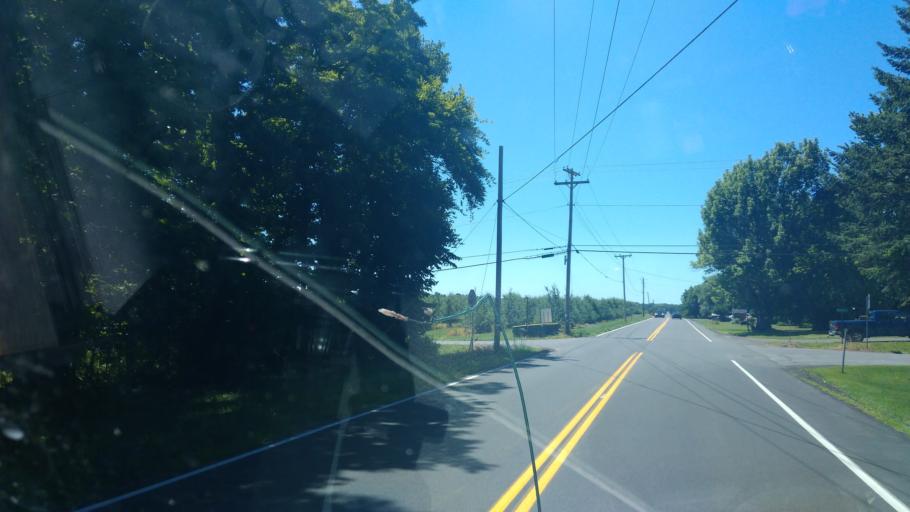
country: US
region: New York
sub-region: Wayne County
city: Sodus
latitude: 43.2361
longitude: -76.9824
